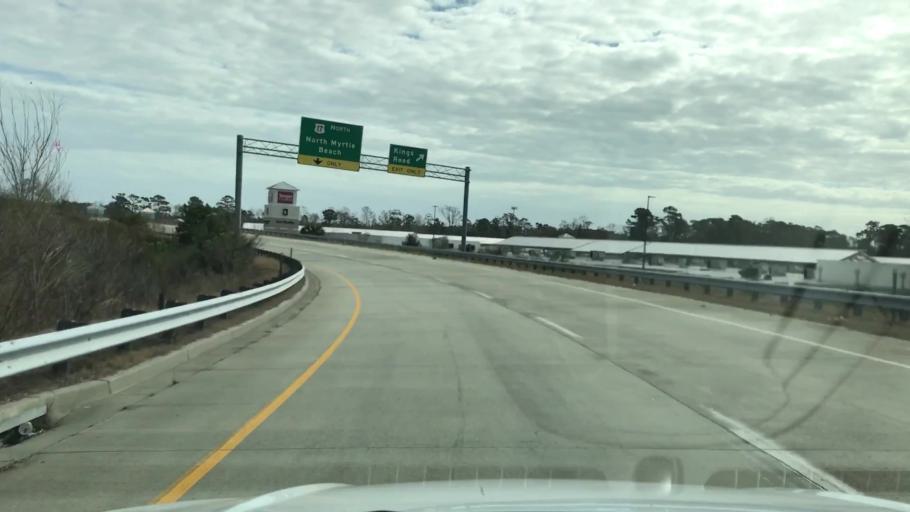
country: US
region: South Carolina
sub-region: Horry County
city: North Myrtle Beach
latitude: 33.7858
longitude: -78.7763
